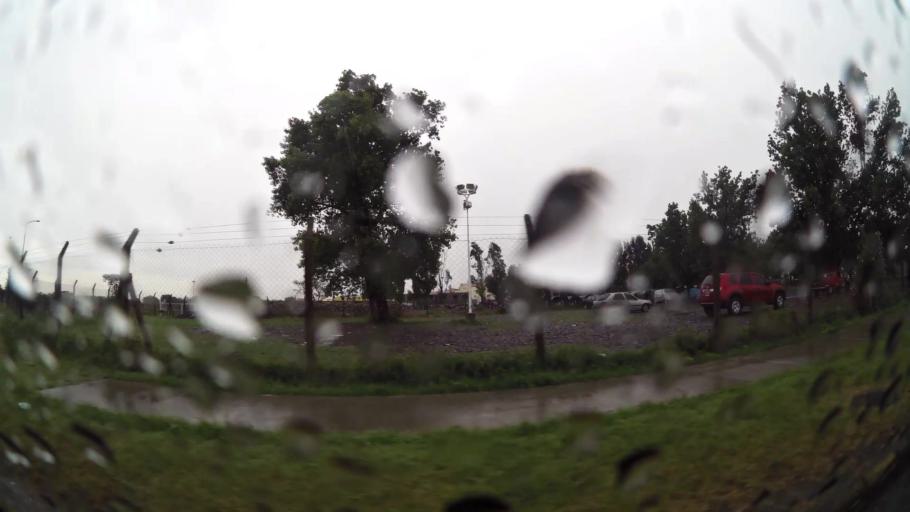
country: AR
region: Buenos Aires F.D.
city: Villa Lugano
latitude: -34.6664
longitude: -58.4551
